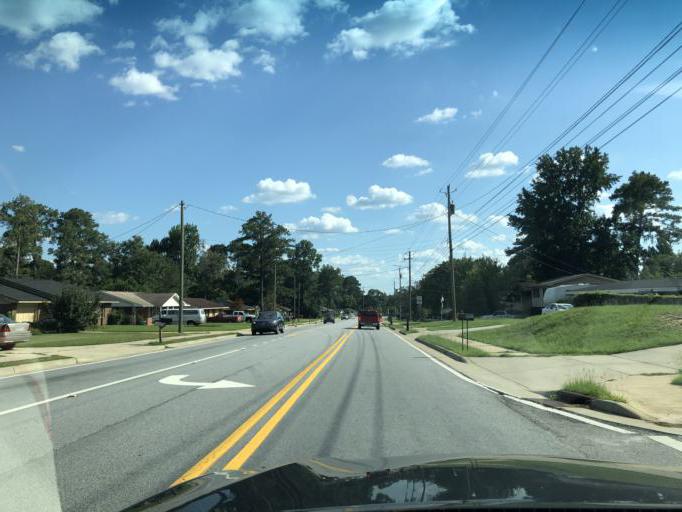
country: US
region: Georgia
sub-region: Muscogee County
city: Columbus
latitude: 32.5384
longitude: -84.9239
